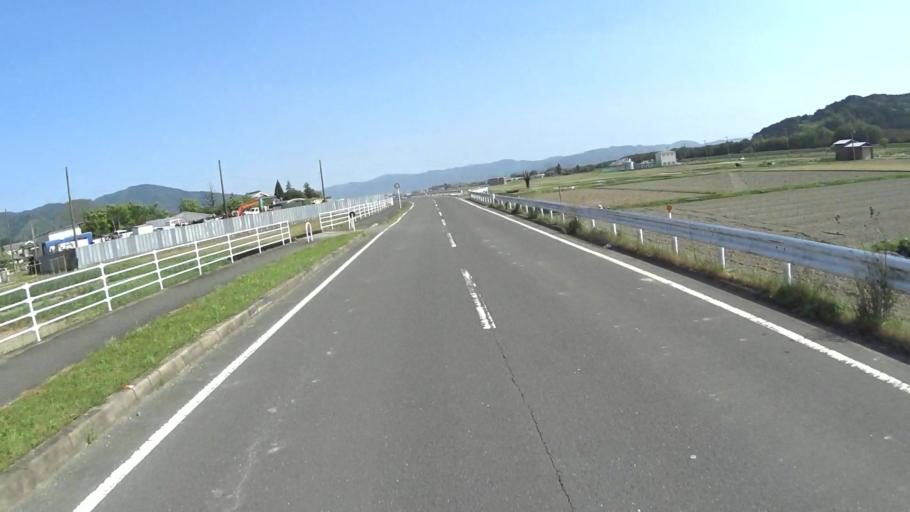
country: JP
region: Kyoto
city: Kameoka
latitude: 35.0715
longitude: 135.5460
